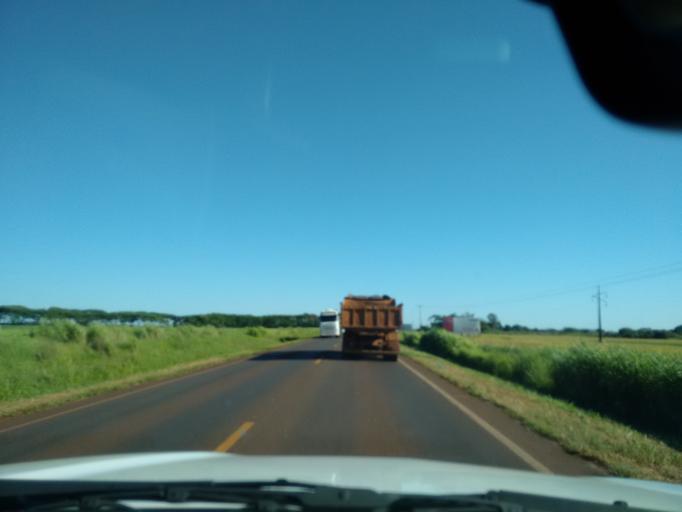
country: BR
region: Mato Grosso do Sul
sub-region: Dourados
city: Dourados
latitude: -22.3049
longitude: -54.8205
